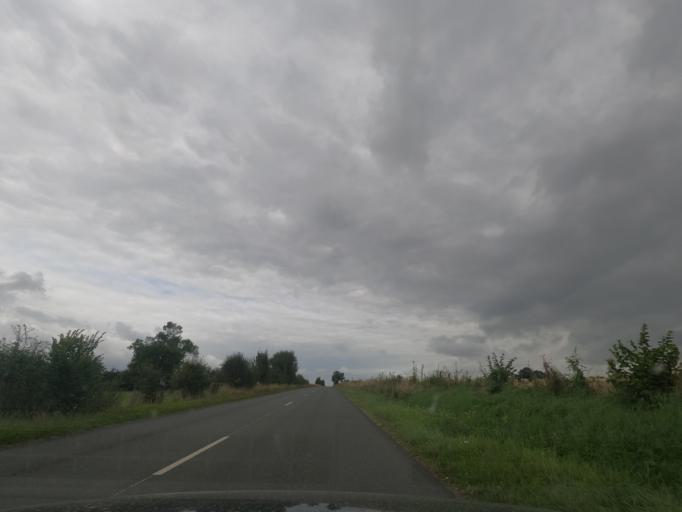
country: FR
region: Lower Normandy
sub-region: Departement de l'Orne
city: Ecouche
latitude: 48.7163
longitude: -0.0941
